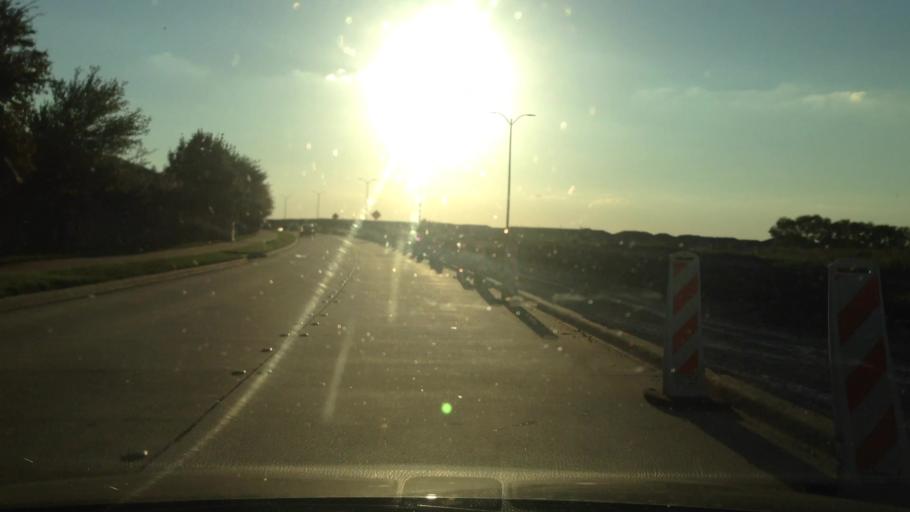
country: US
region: Texas
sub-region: Denton County
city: Little Elm
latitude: 33.1461
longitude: -96.9026
